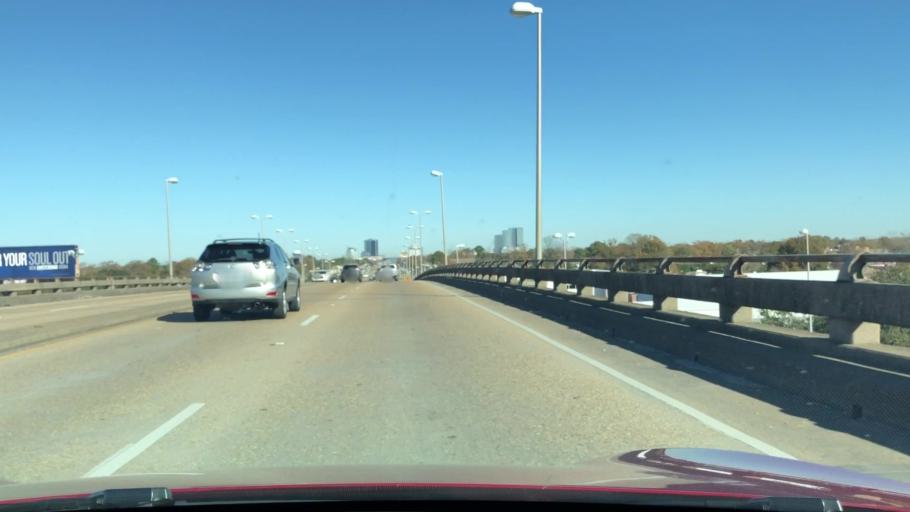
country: US
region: Louisiana
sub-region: Jefferson Parish
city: Metairie Terrace
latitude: 29.9748
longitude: -90.1563
